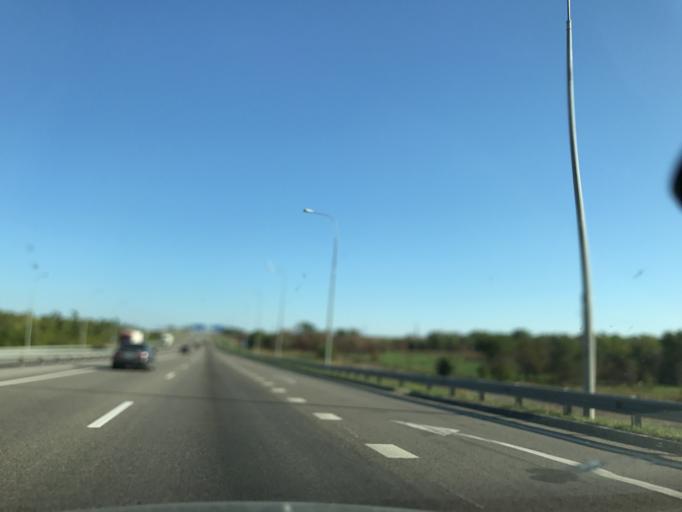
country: RU
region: Rostov
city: Glubokiy
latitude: 48.5373
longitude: 40.3456
